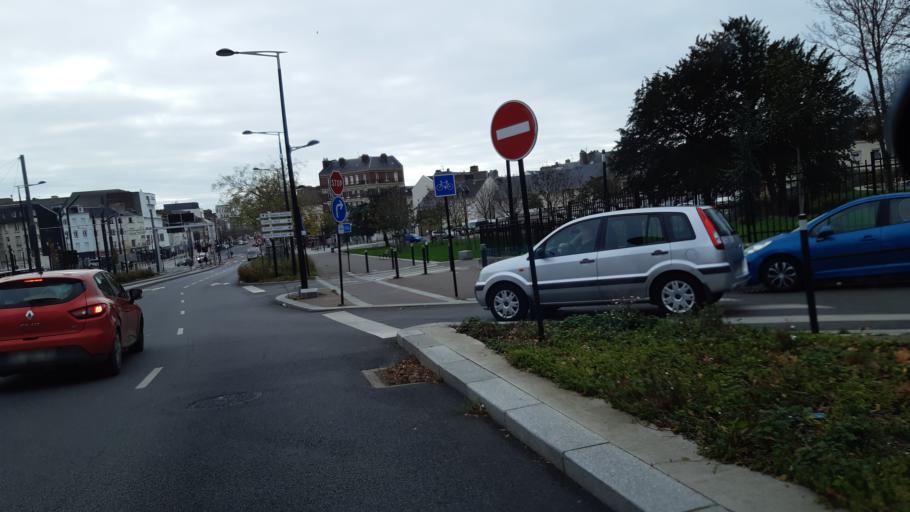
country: FR
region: Haute-Normandie
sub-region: Departement de la Seine-Maritime
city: Le Havre
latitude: 49.5012
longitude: 0.1307
